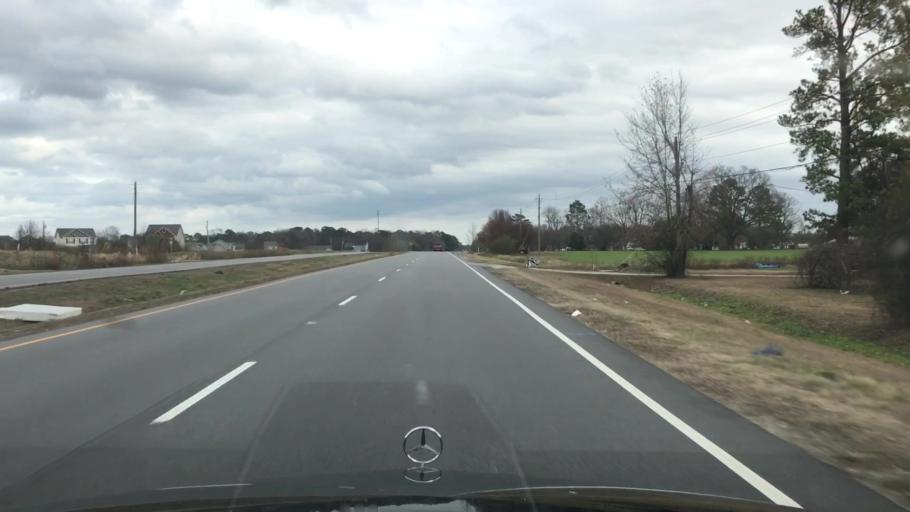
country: US
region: North Carolina
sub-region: Onslow County
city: Richlands
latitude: 34.9171
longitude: -77.6076
